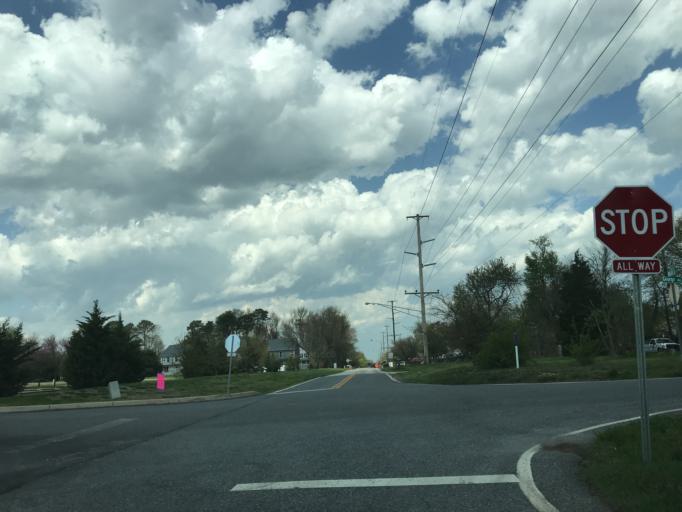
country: US
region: Maryland
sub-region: Anne Arundel County
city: Odenton
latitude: 39.1042
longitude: -76.6891
